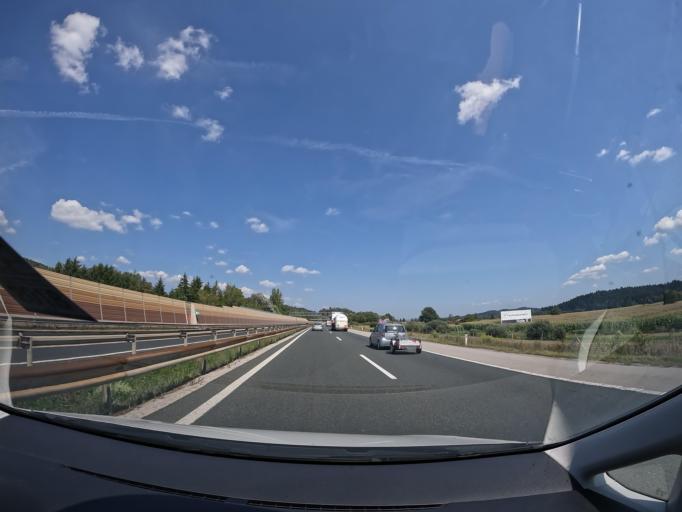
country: SI
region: Log-Dragomer
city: Log pri Brezovici
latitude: 46.0009
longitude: 14.3463
